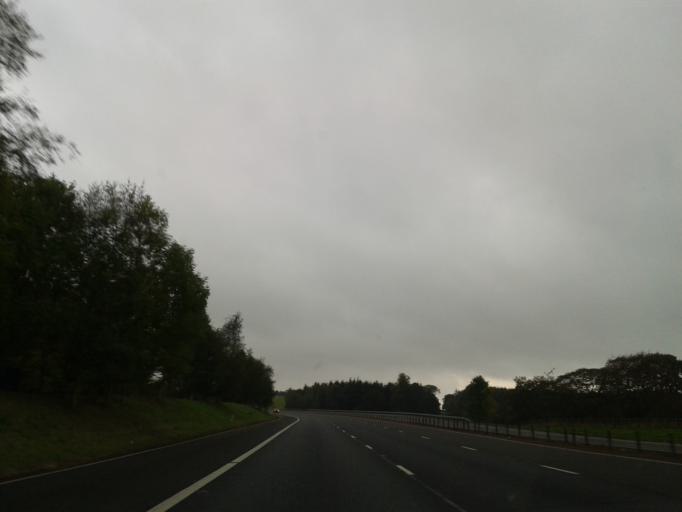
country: GB
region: Scotland
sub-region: Dumfries and Galloway
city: Lochmaben
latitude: 55.1817
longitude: -3.4052
